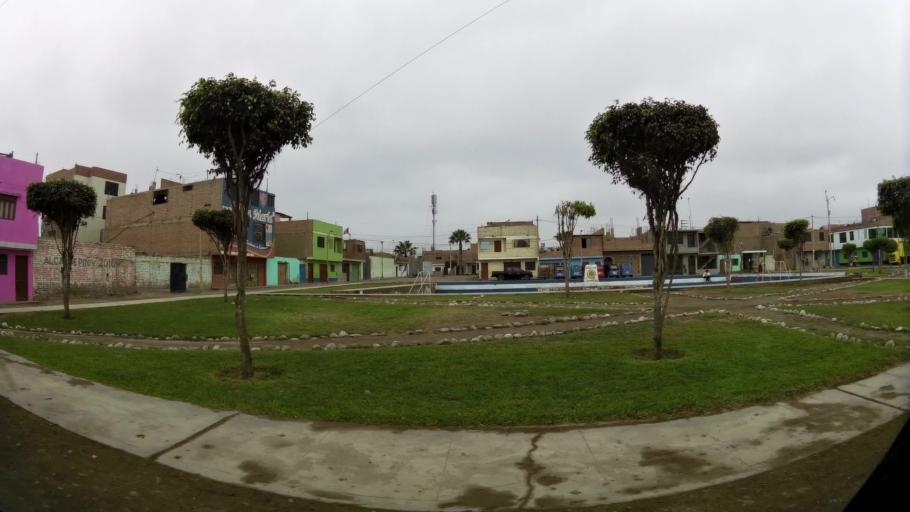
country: PE
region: Lima
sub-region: Barranca
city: Barranca
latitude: -10.7476
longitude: -77.7546
